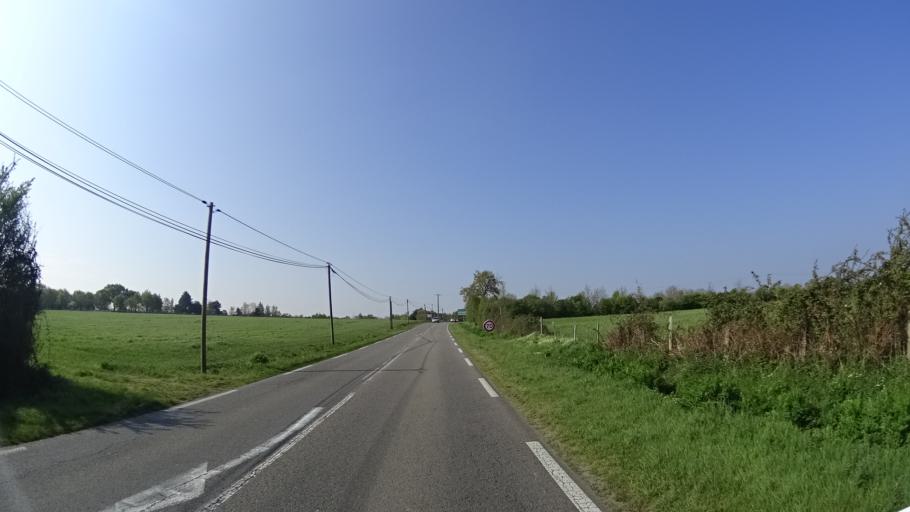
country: FR
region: Pays de la Loire
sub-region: Departement de la Loire-Atlantique
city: Sainte-Pazanne
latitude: 47.1084
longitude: -1.7872
